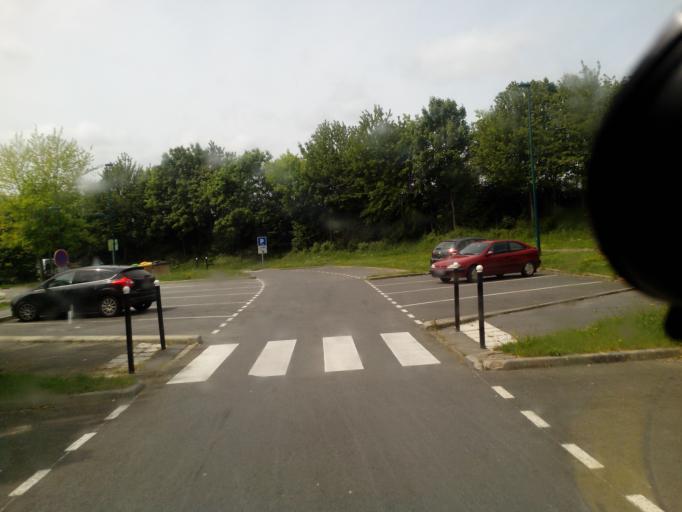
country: FR
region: Brittany
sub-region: Departement d'Ille-et-Vilaine
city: Chatillon-sur-Seiche
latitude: 48.0569
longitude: -1.6793
